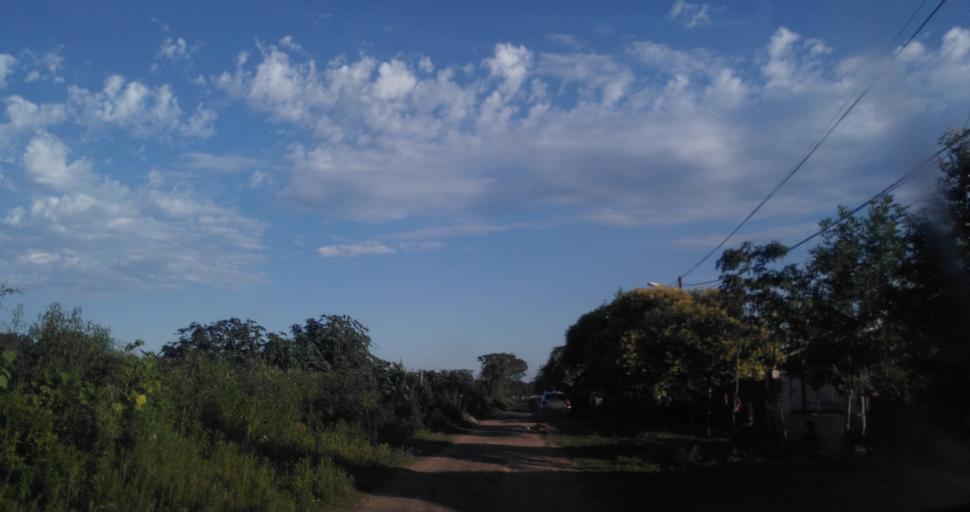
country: AR
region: Chaco
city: Fontana
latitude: -27.4130
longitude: -59.0249
